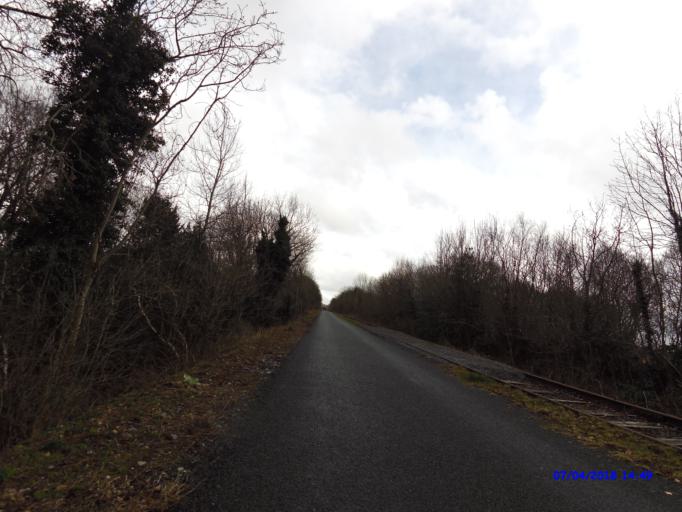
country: IE
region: Leinster
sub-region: An Iarmhi
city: Athlone
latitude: 53.4157
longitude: -7.8624
